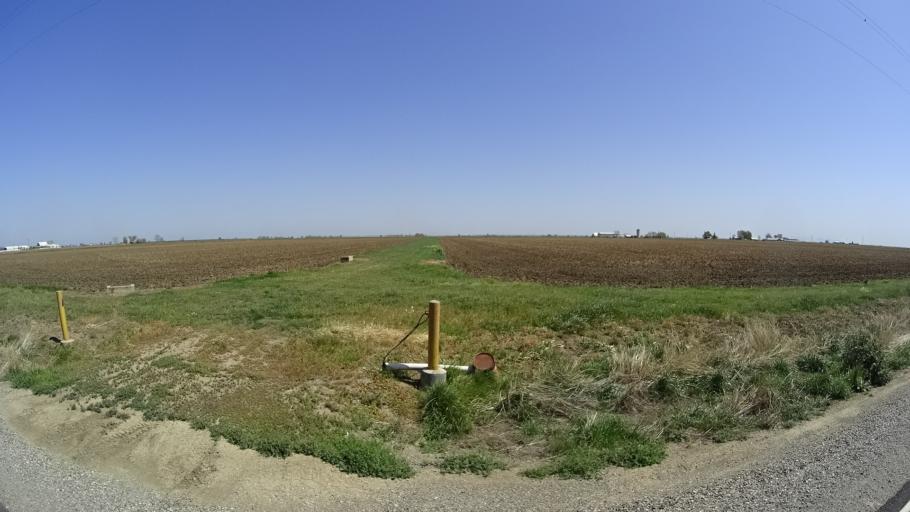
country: US
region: California
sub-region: Glenn County
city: Willows
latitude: 39.4977
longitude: -122.1367
